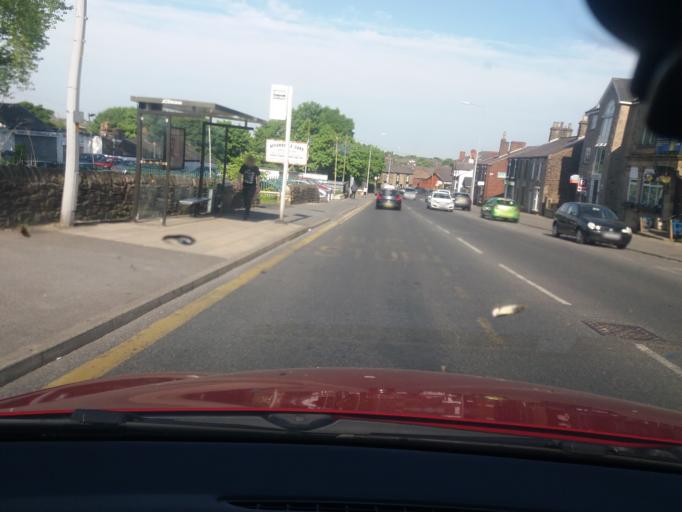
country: GB
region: England
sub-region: Borough of Bolton
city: Horwich
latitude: 53.5990
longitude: -2.5435
